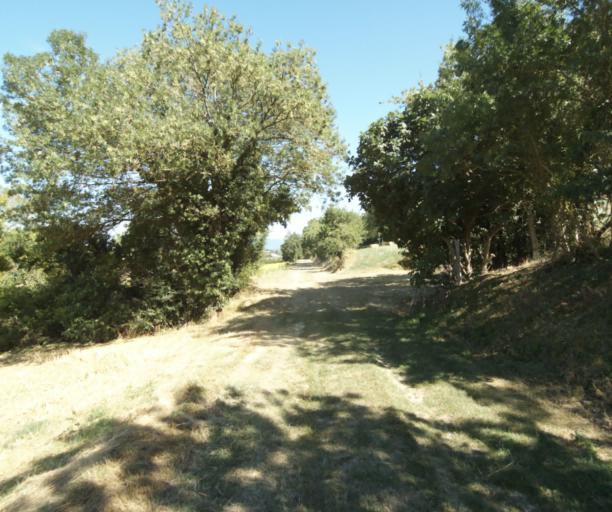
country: FR
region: Midi-Pyrenees
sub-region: Departement de la Haute-Garonne
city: Saint-Felix-Lauragais
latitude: 43.4952
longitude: 1.8968
